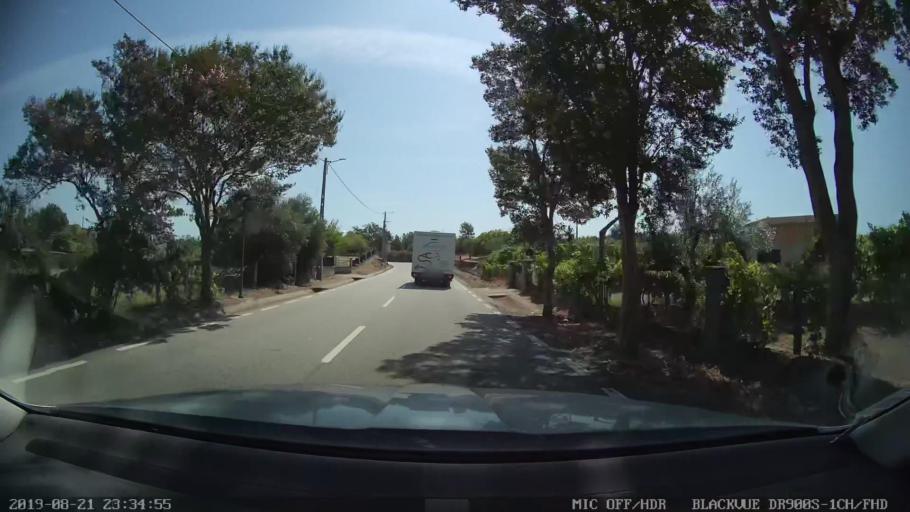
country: PT
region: Guarda
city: Alcains
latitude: 39.8791
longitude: -7.3940
